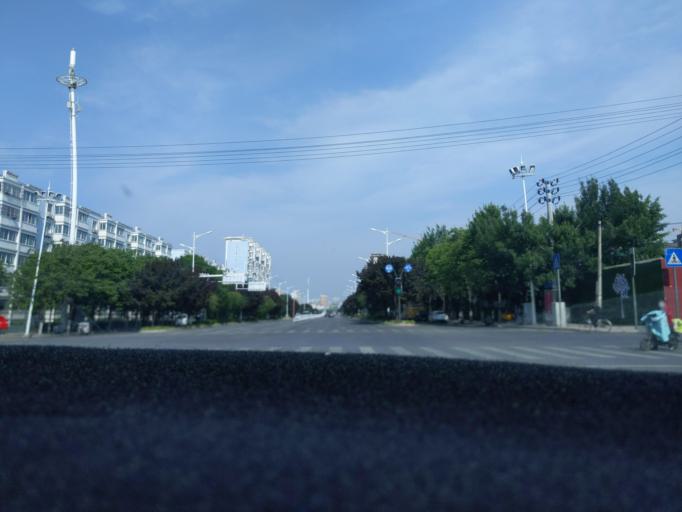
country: CN
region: Henan Sheng
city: Puyang
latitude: 35.7569
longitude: 115.0395
